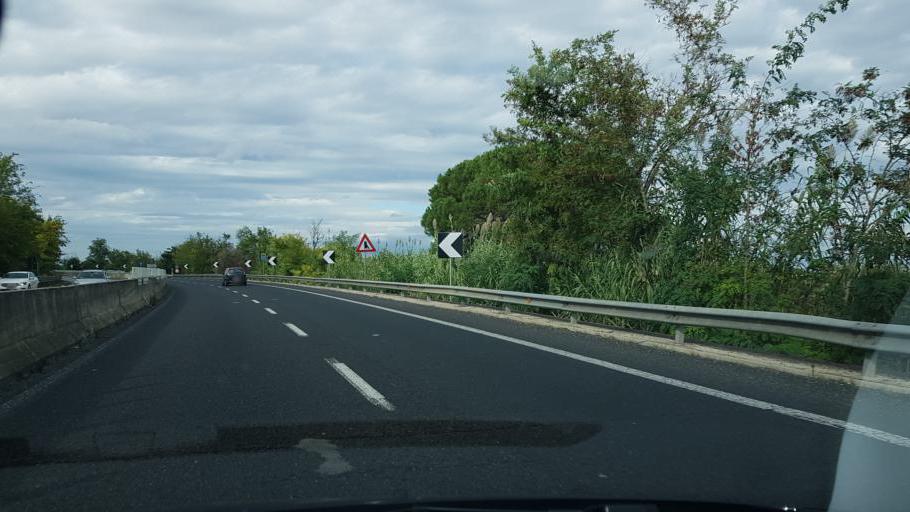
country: IT
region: Apulia
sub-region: Provincia di Lecce
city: Cavallino
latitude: 40.3121
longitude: 18.1898
